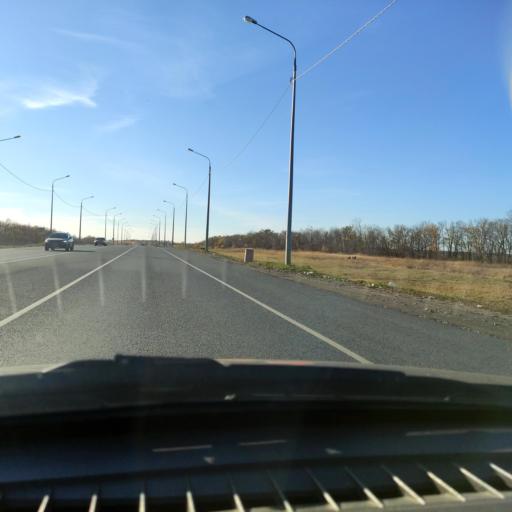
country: RU
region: Samara
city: Mezhdurechensk
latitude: 53.2468
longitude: 49.0077
